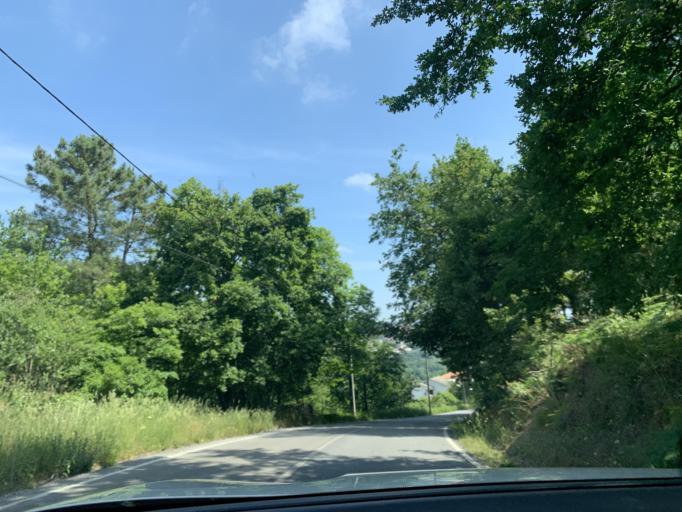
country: PT
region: Viseu
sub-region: Viseu
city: Viseu
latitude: 40.6471
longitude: -7.9408
